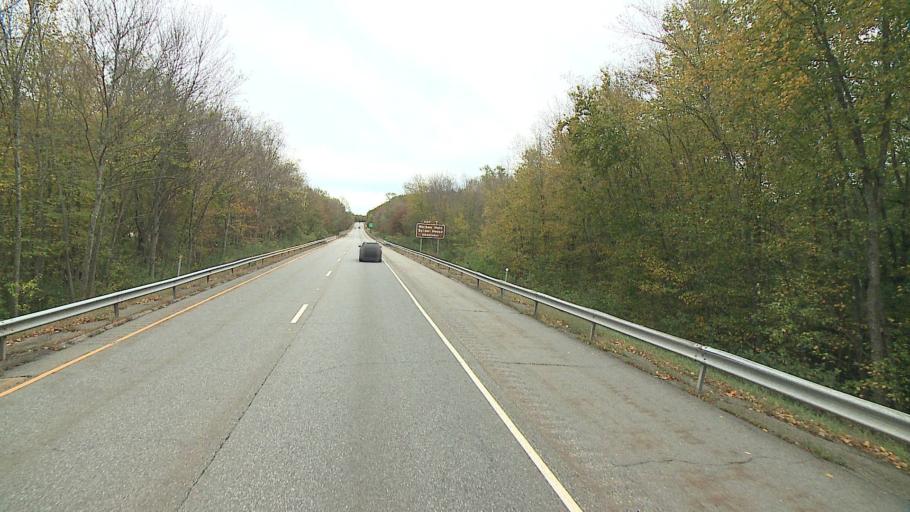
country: US
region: Connecticut
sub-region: Middlesex County
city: East Haddam
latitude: 41.4250
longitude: -72.5036
